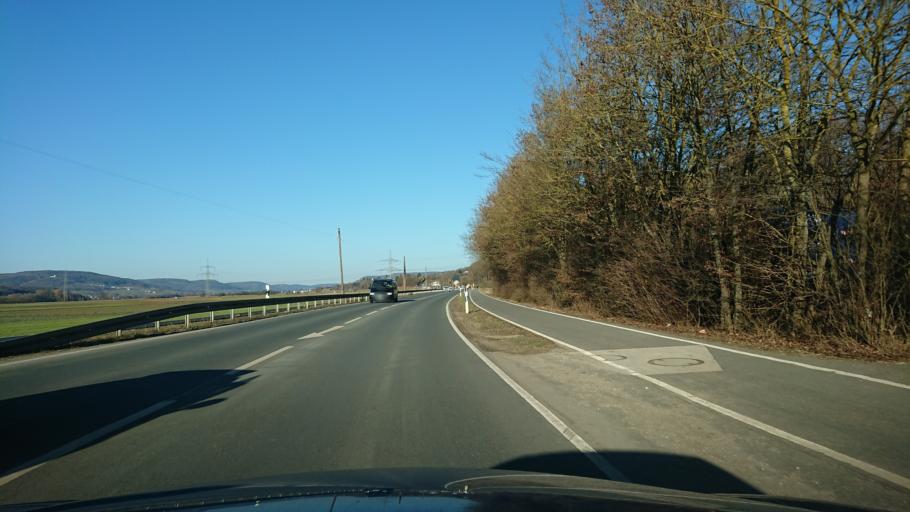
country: DE
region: Bavaria
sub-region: Upper Franconia
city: Wiesenthau
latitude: 49.7082
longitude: 11.1196
